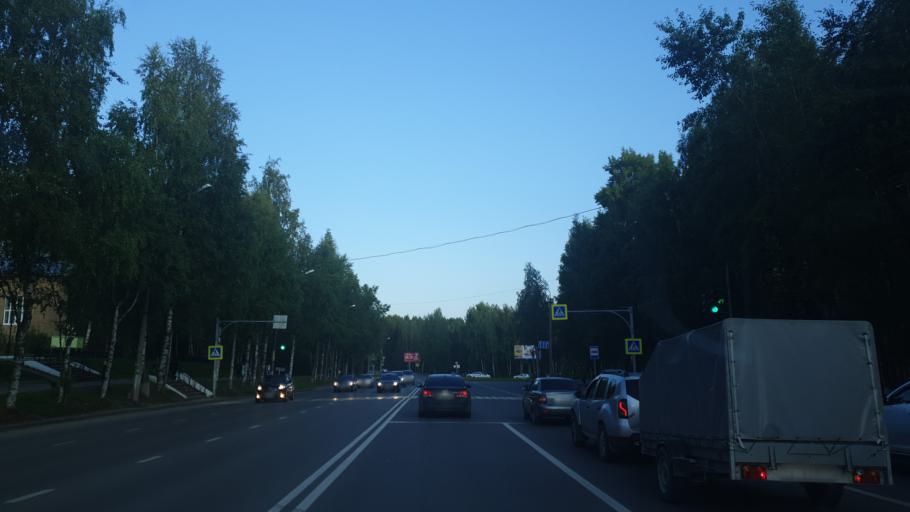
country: RU
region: Komi Republic
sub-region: Syktyvdinskiy Rayon
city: Syktyvkar
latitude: 61.6620
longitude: 50.8180
